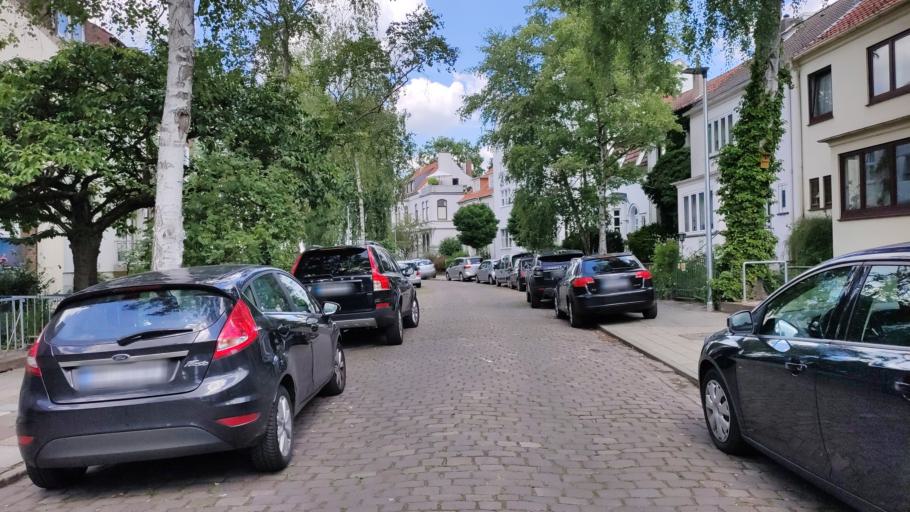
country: DE
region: Bremen
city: Bremen
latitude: 53.0850
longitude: 8.8427
